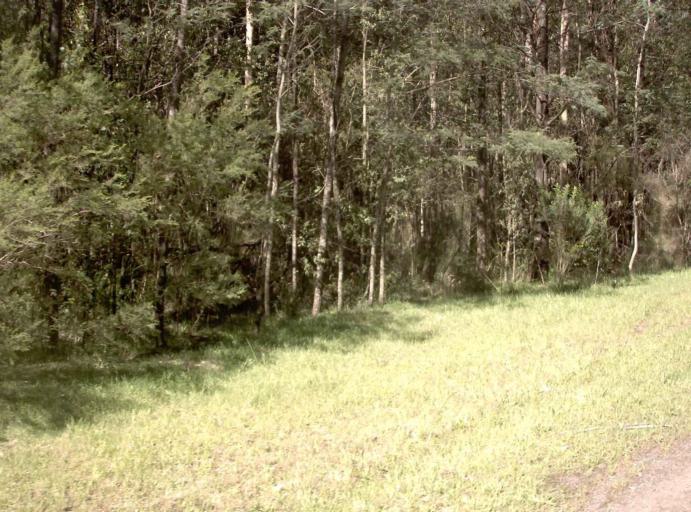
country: AU
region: Victoria
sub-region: Yarra Ranges
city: Millgrove
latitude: -37.8806
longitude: 145.8554
